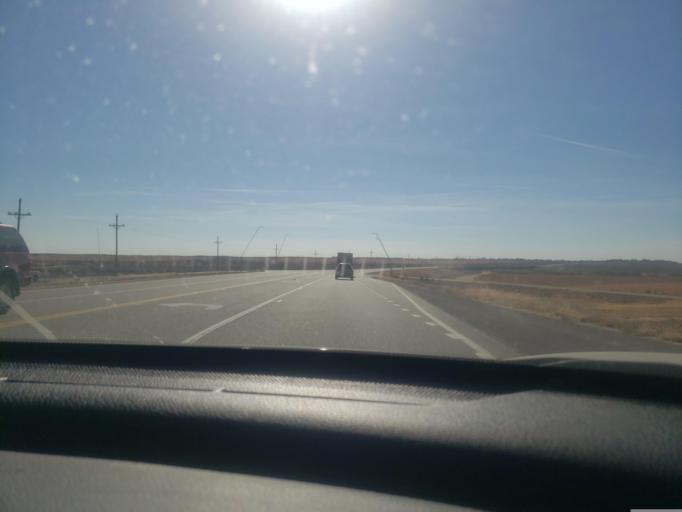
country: US
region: Kansas
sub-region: Finney County
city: Garden City
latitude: 37.9557
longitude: -100.8402
